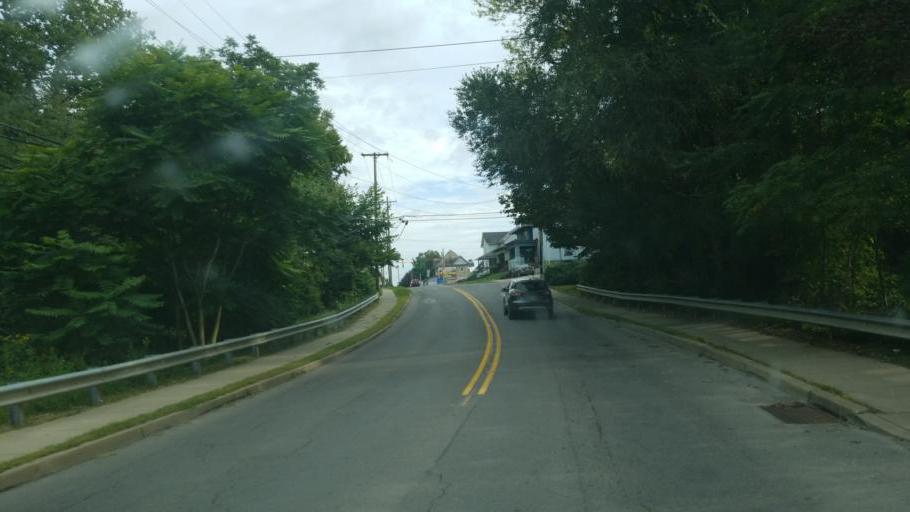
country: US
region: Pennsylvania
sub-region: Mercer County
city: Greenville
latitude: 41.4091
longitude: -80.3846
